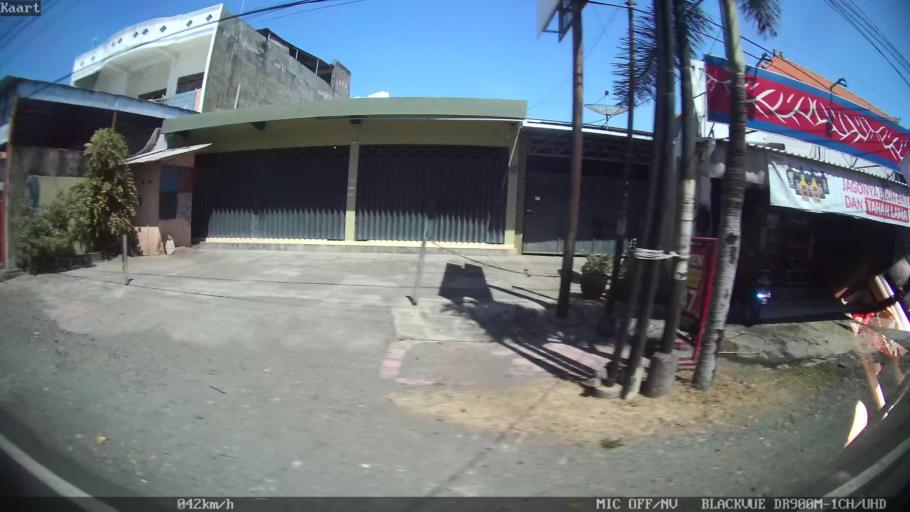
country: ID
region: Bali
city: Banjar Sidayu
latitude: -8.0960
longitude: 115.1106
